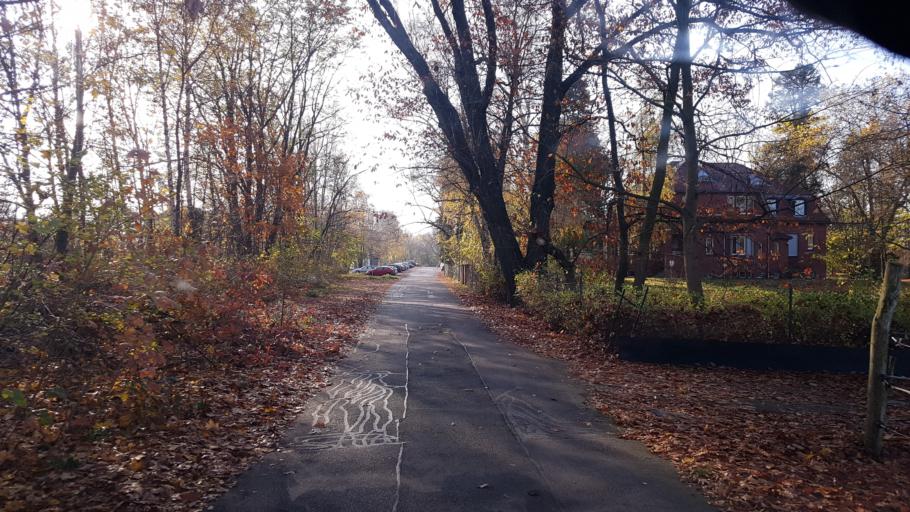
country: DE
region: Brandenburg
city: Schipkau
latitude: 51.5562
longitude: 13.8893
